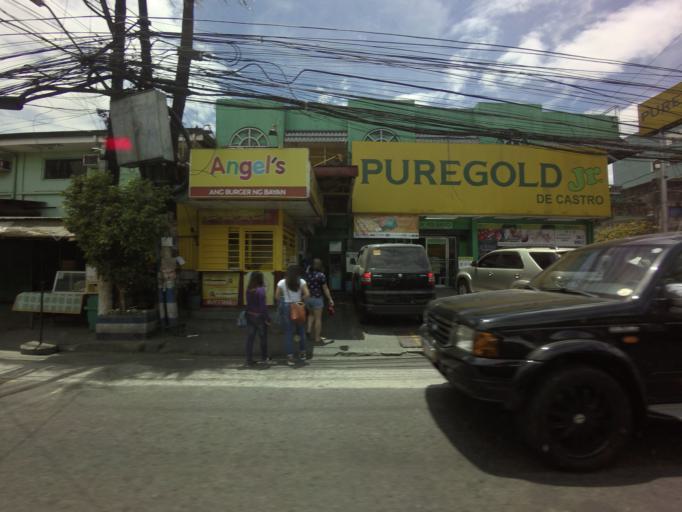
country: PH
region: Calabarzon
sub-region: Province of Rizal
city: Cainta
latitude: 14.5888
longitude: 121.0974
